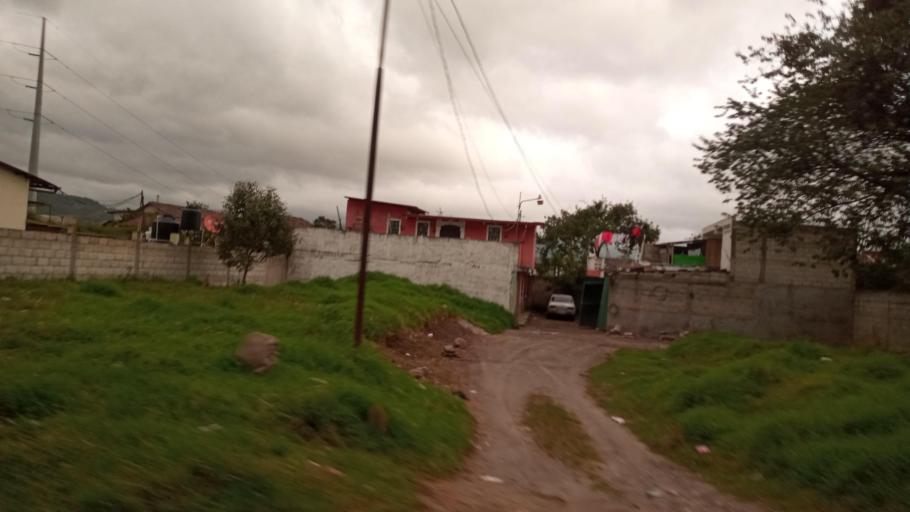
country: GT
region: Quetzaltenango
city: Quetzaltenango
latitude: 14.8254
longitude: -91.5349
